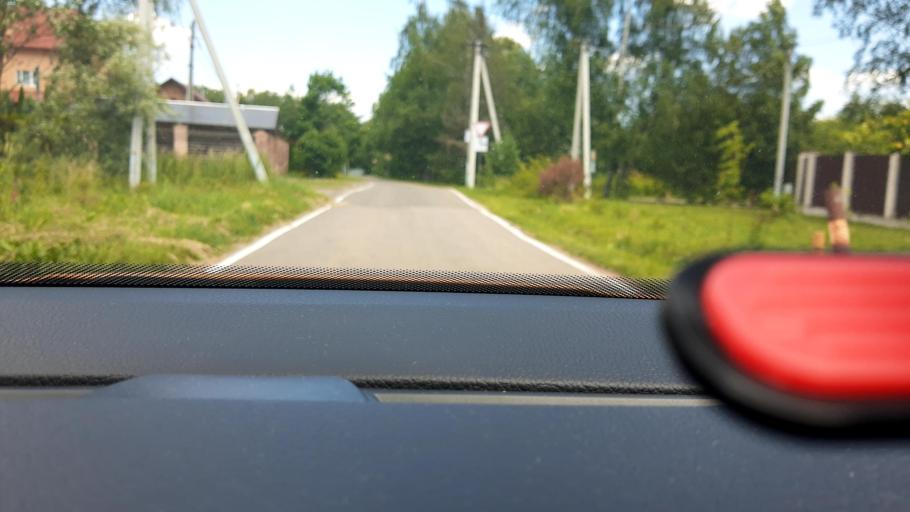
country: RU
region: Moskovskaya
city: Firsanovka
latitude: 55.9051
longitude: 37.2189
